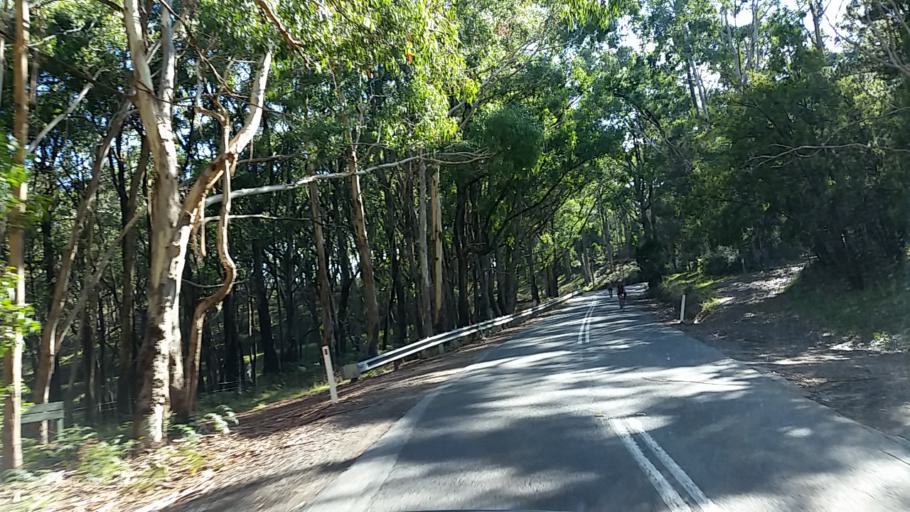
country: AU
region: South Australia
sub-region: Adelaide Hills
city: Crafers
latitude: -34.9610
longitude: 138.7138
